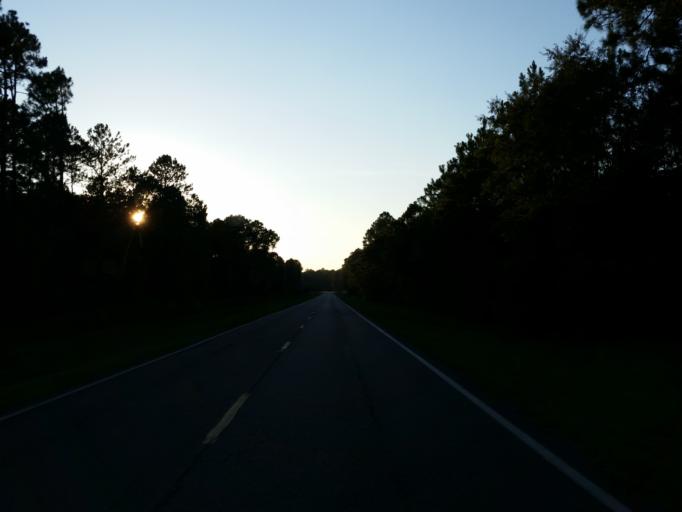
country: US
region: Georgia
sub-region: Berrien County
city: Nashville
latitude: 31.1825
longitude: -83.1423
